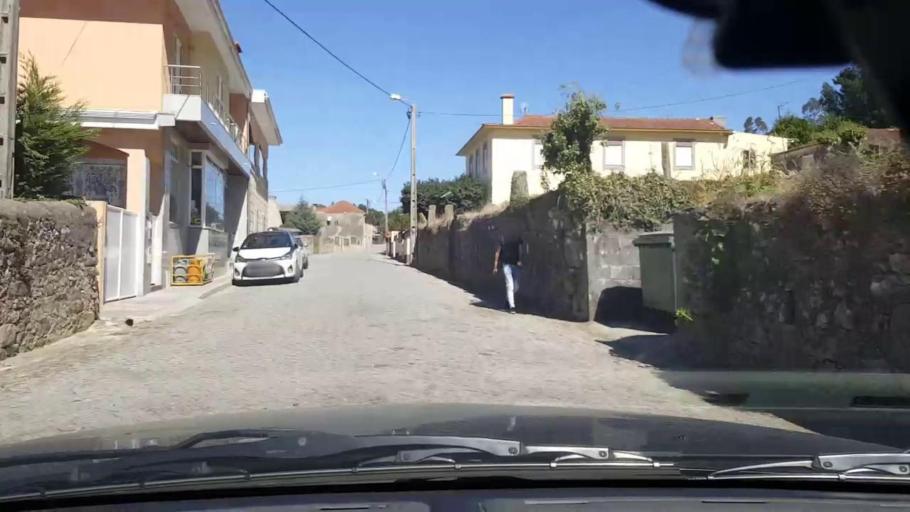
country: PT
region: Porto
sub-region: Maia
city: Gemunde
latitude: 41.3294
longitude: -8.6441
